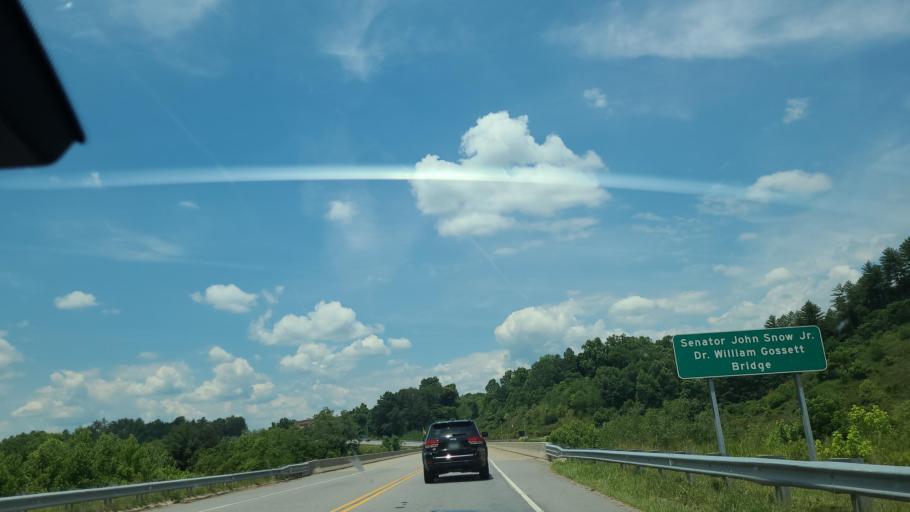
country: US
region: North Carolina
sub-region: Cherokee County
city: Murphy
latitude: 35.0770
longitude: -84.0257
